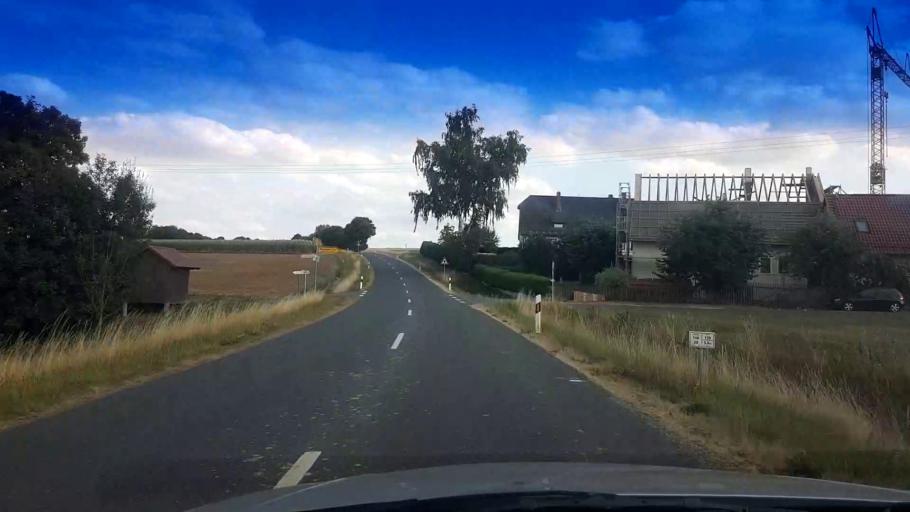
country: DE
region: Bavaria
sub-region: Upper Palatinate
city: Waldsassen
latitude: 50.0165
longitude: 12.3599
